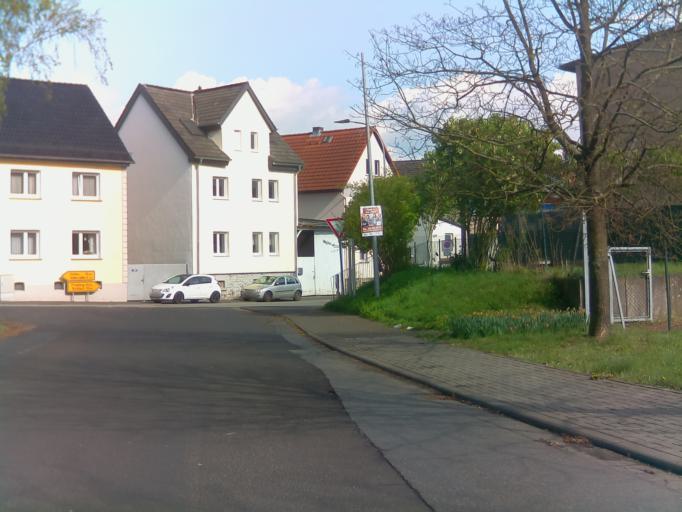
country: DE
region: Hesse
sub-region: Regierungsbezirk Giessen
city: Langgons
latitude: 50.5008
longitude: 8.6567
